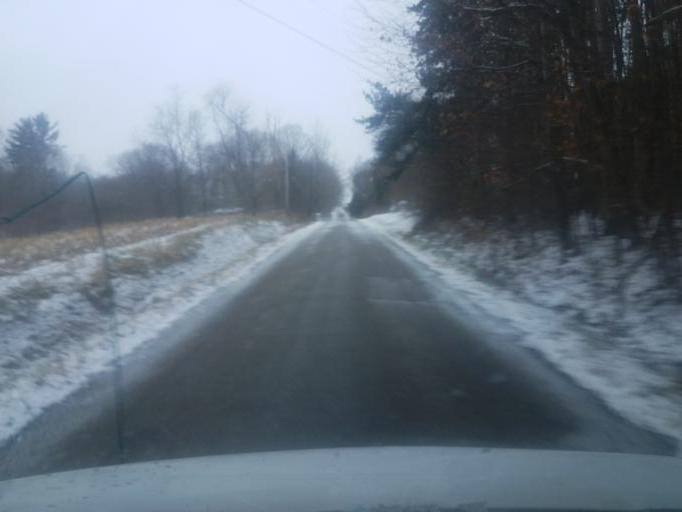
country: US
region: Ohio
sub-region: Sandusky County
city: Bellville
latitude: 40.6056
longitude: -82.4198
